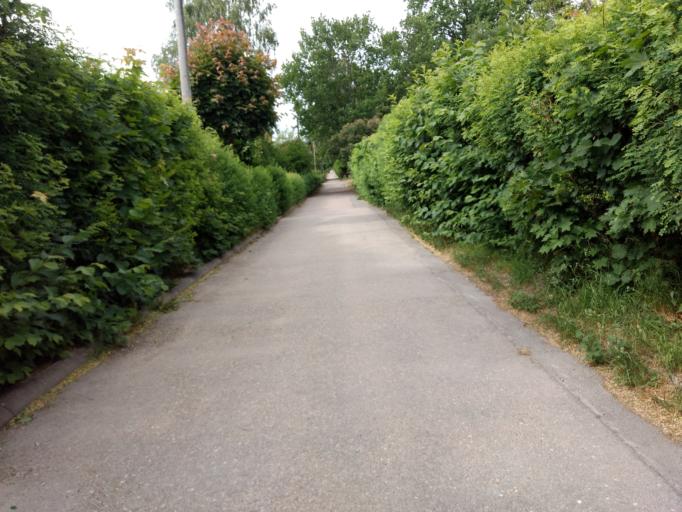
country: SE
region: Stockholm
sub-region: Upplands Vasby Kommun
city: Upplands Vaesby
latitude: 59.5235
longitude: 17.9080
